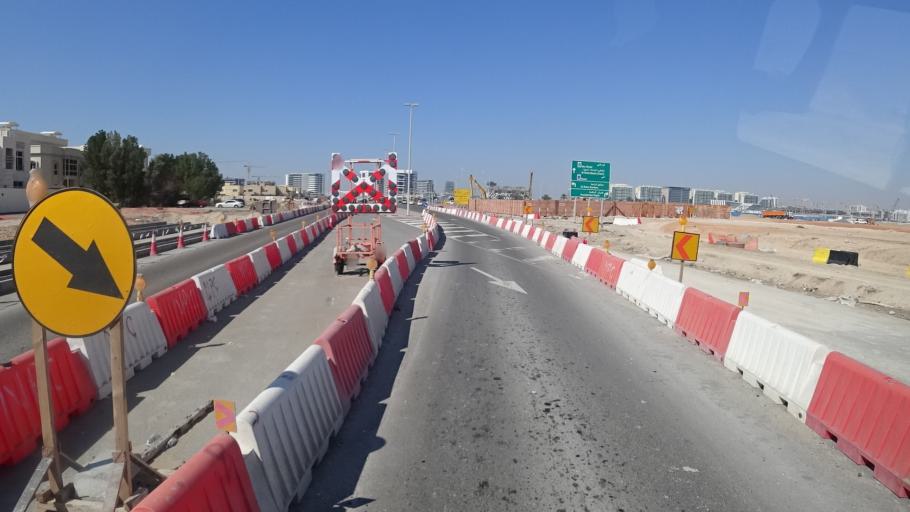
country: AE
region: Abu Dhabi
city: Abu Dhabi
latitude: 24.4386
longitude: 54.6022
